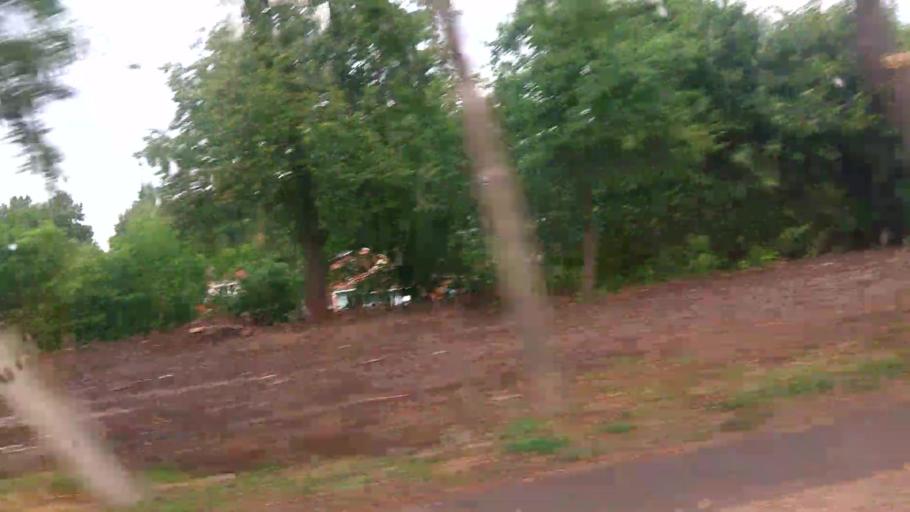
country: RU
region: Moskovskaya
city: Zaraysk
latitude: 54.7551
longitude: 38.8691
